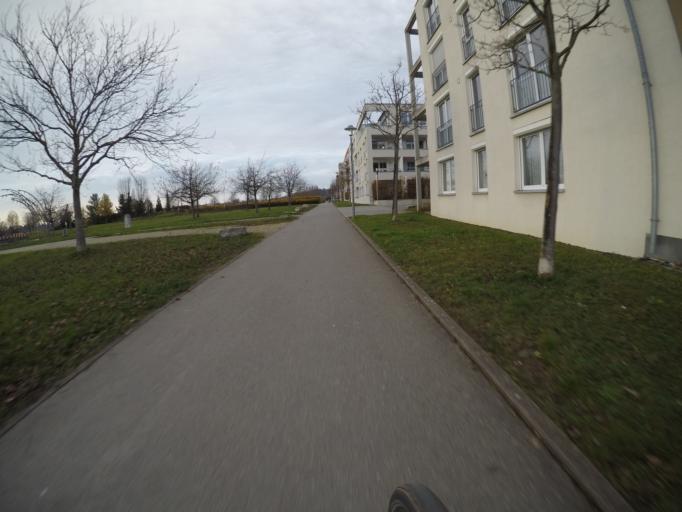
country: DE
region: Baden-Wuerttemberg
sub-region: Regierungsbezirk Stuttgart
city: Ostfildern
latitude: 48.7174
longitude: 9.2669
